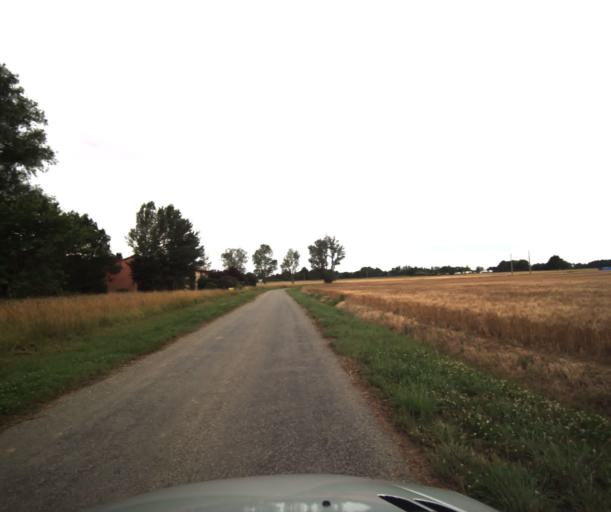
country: FR
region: Midi-Pyrenees
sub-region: Departement de la Haute-Garonne
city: Labarthe-sur-Leze
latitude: 43.4675
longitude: 1.4102
